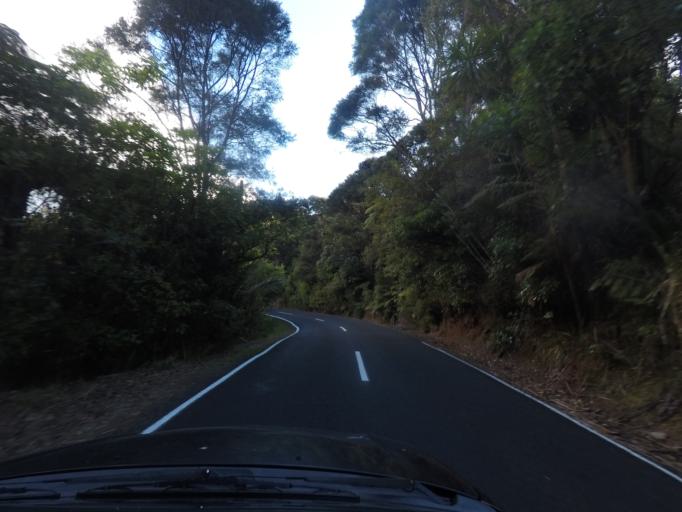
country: NZ
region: Auckland
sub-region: Auckland
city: Titirangi
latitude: -36.9343
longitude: 174.6187
